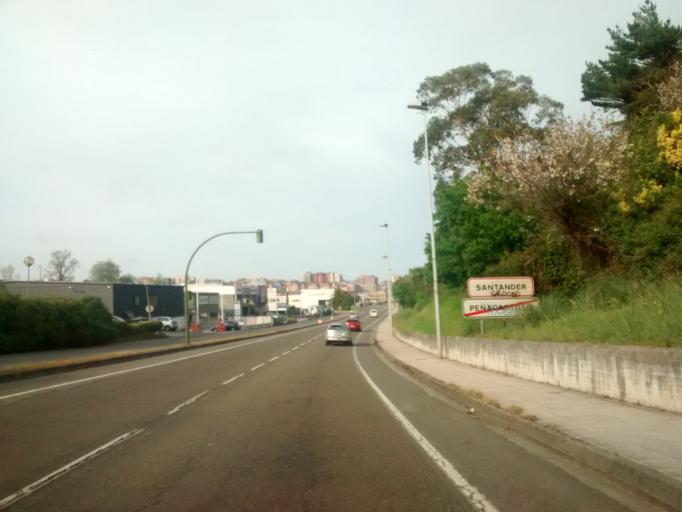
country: ES
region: Cantabria
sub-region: Provincia de Cantabria
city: Santa Cruz de Bezana
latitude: 43.4496
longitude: -3.8623
